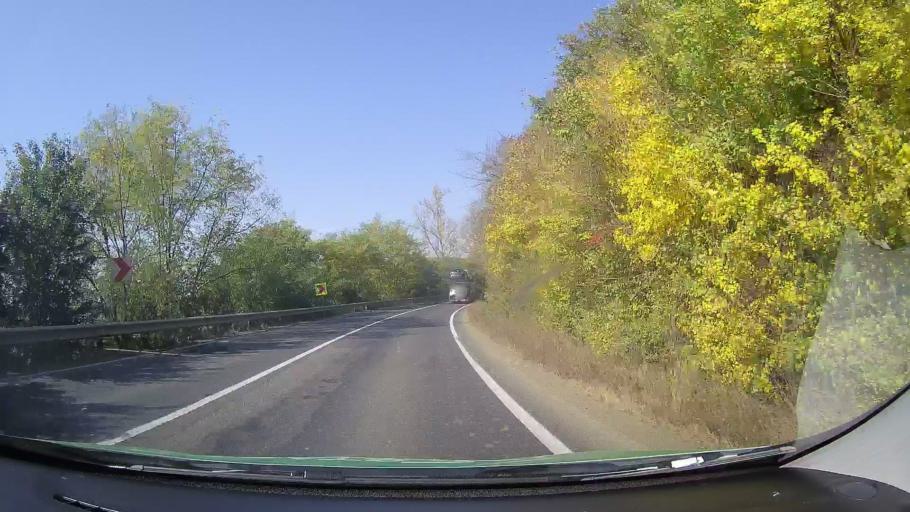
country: RO
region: Arad
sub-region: Comuna Varadia de Mures
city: Varadia de Mures
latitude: 46.0260
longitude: 22.1241
